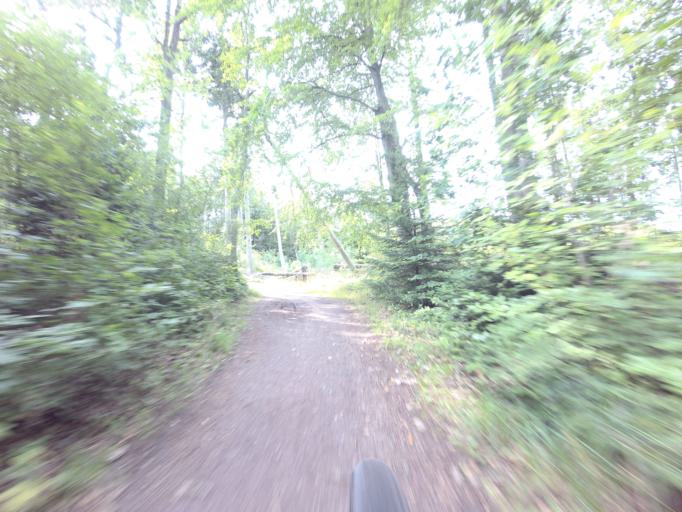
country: DK
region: North Denmark
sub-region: Hjorring Kommune
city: Sindal
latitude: 57.5836
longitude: 10.1814
